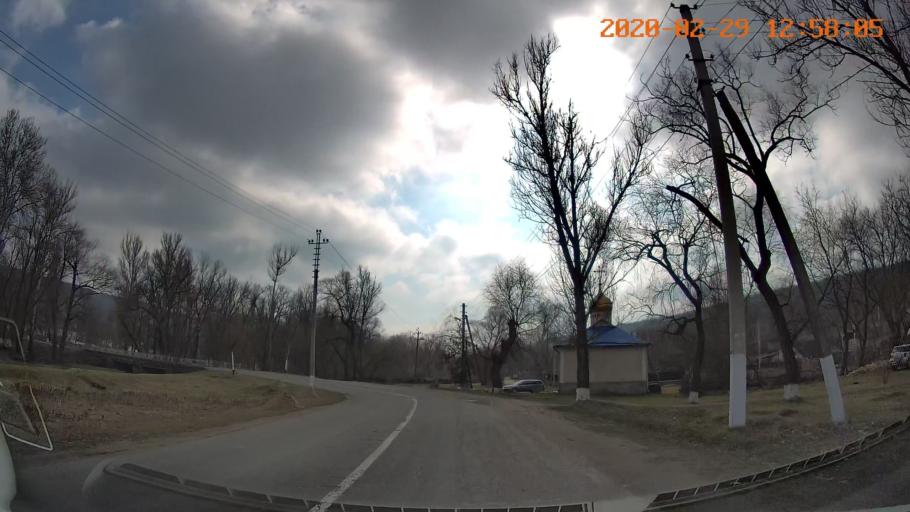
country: MD
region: Telenesti
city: Camenca
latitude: 48.0715
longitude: 28.7177
